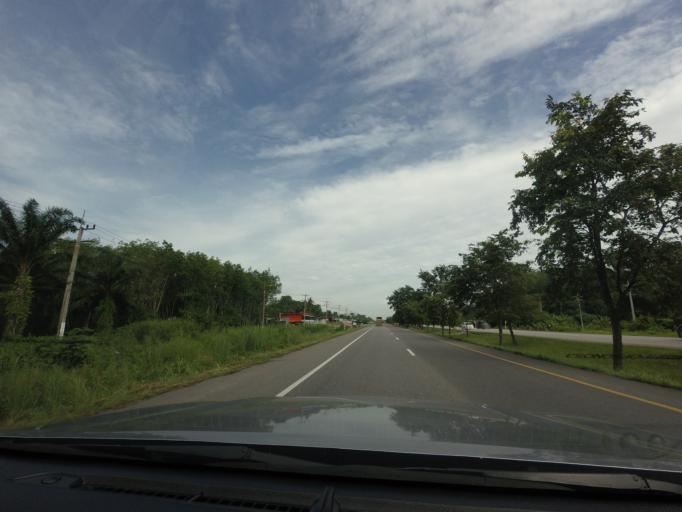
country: TH
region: Nakhon Si Thammarat
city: Na Bon
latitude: 8.2907
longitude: 99.5219
